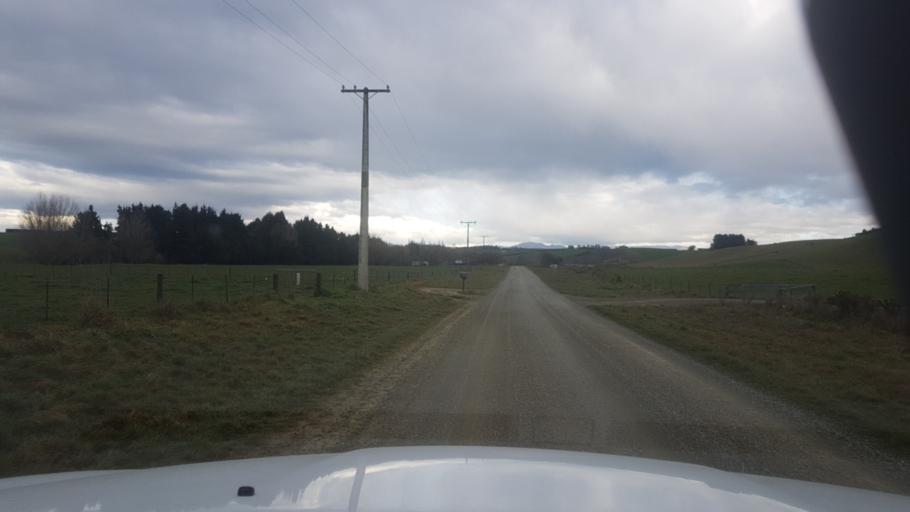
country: NZ
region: Canterbury
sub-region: Timaru District
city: Pleasant Point
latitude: -44.3380
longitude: 171.1781
